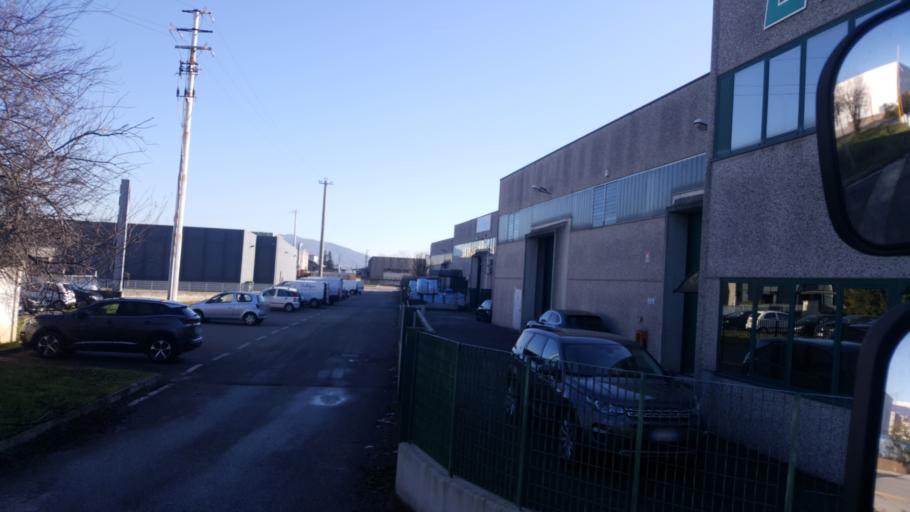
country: IT
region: Lombardy
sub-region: Provincia di Brescia
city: Castegnato
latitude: 45.5491
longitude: 10.1196
